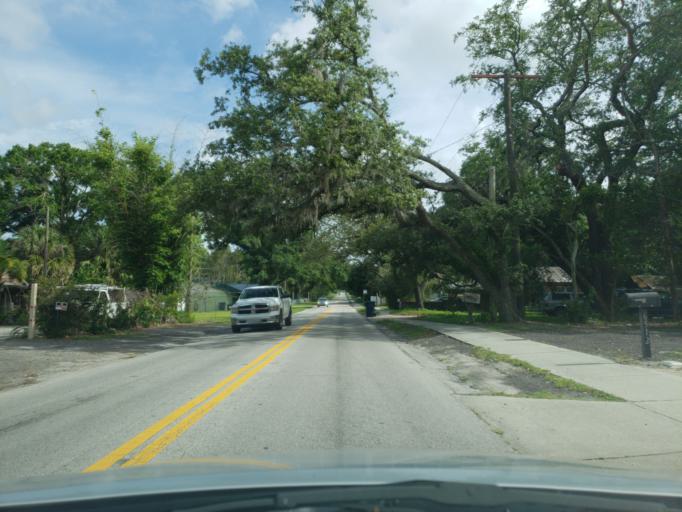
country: US
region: Florida
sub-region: Hillsborough County
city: Egypt Lake-Leto
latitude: 28.0068
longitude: -82.4761
